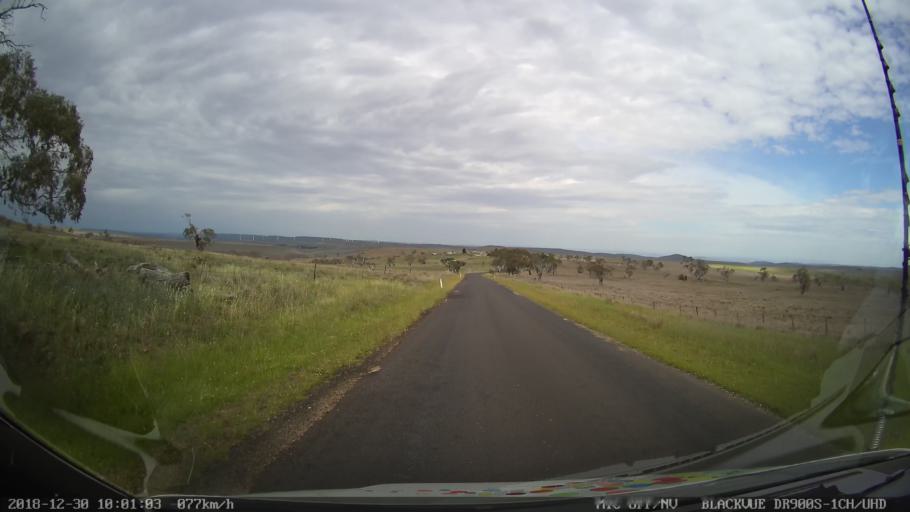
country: AU
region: New South Wales
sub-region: Cooma-Monaro
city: Cooma
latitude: -36.5139
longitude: 149.1918
